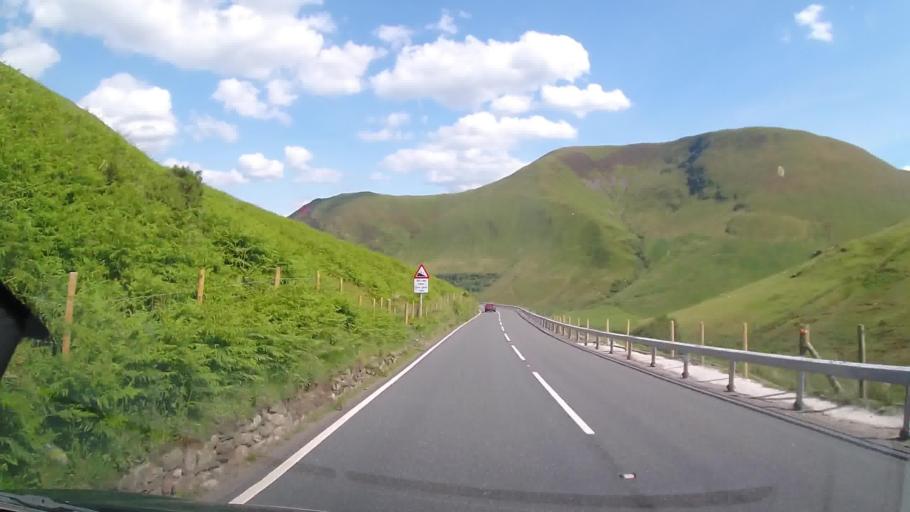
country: GB
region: Wales
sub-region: Gwynedd
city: Corris
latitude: 52.7341
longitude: -3.7633
